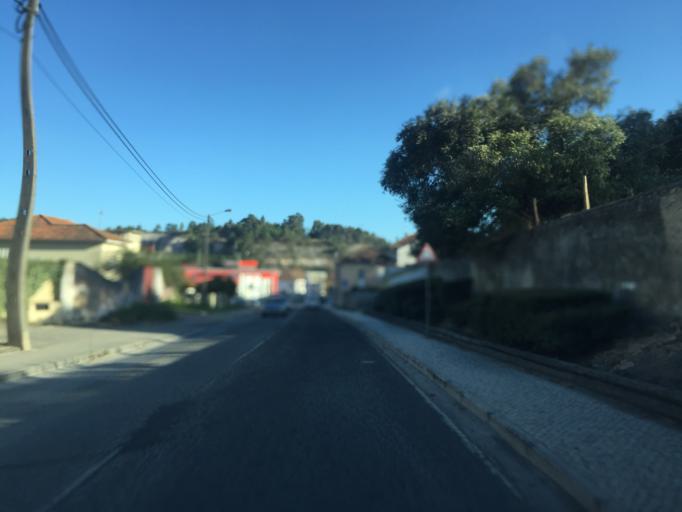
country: PT
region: Lisbon
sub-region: Torres Vedras
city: Torres Vedras
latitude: 39.1033
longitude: -9.2593
